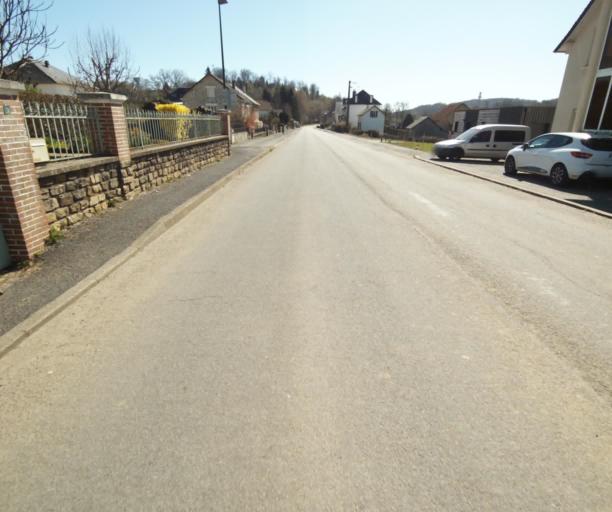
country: FR
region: Limousin
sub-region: Departement de la Correze
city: Seilhac
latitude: 45.3693
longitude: 1.7028
